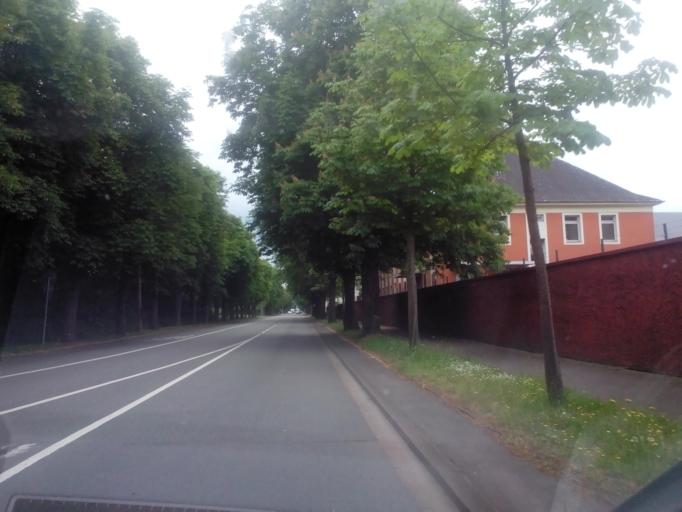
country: DE
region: Saarland
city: Saarlouis
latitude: 49.3160
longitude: 6.7379
